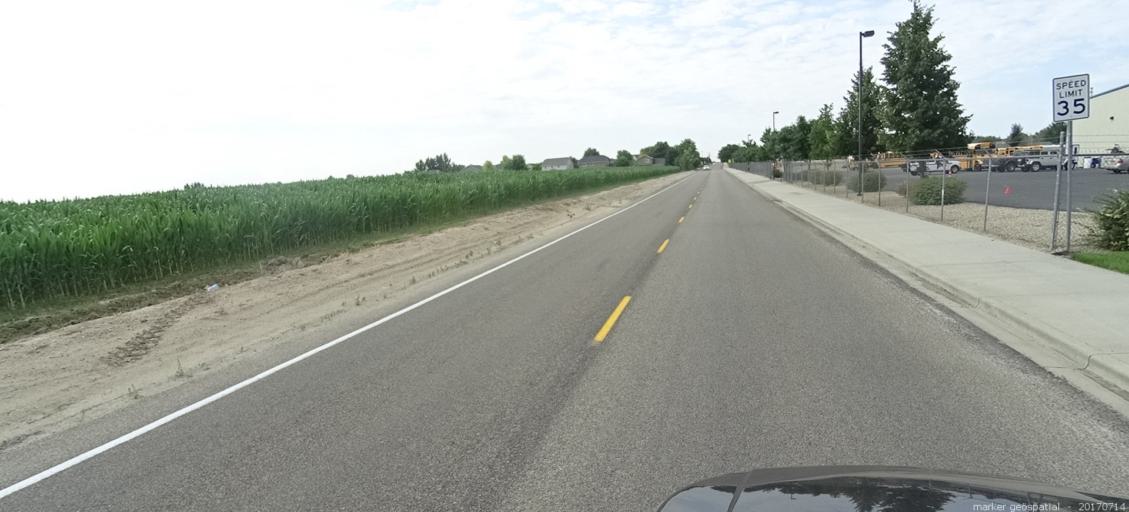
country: US
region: Idaho
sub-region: Ada County
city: Kuna
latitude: 43.4978
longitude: -116.4039
